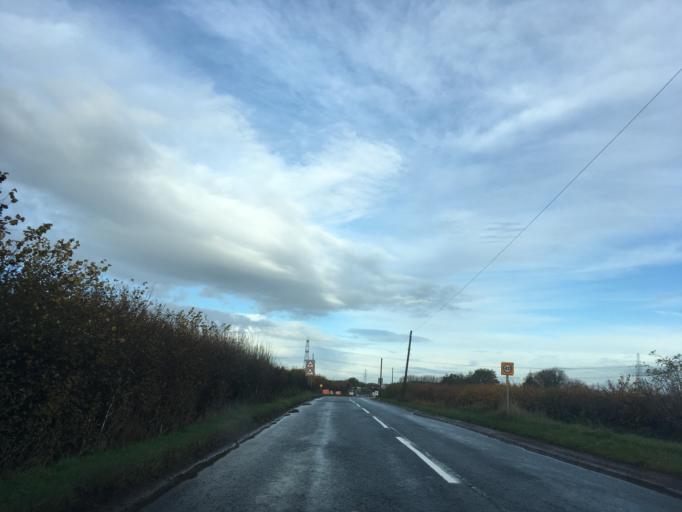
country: GB
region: England
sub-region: South Gloucestershire
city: Winterbourne
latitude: 51.5412
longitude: -2.4878
